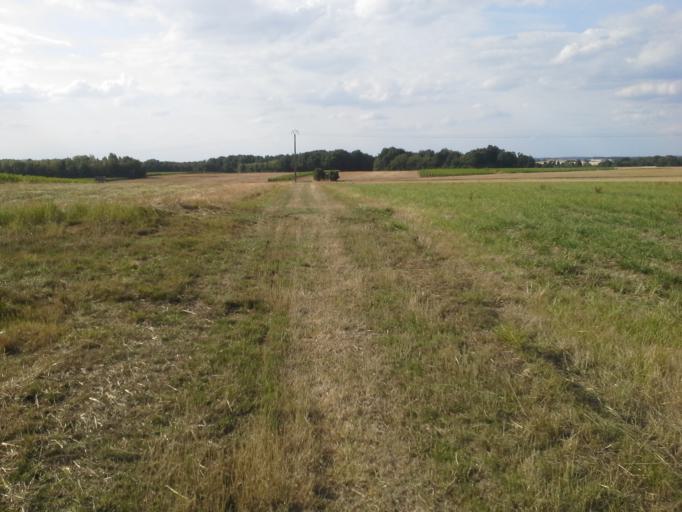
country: FR
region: Centre
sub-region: Departement du Loir-et-Cher
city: Villiers-sur-Loir
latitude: 47.8204
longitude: 1.0002
